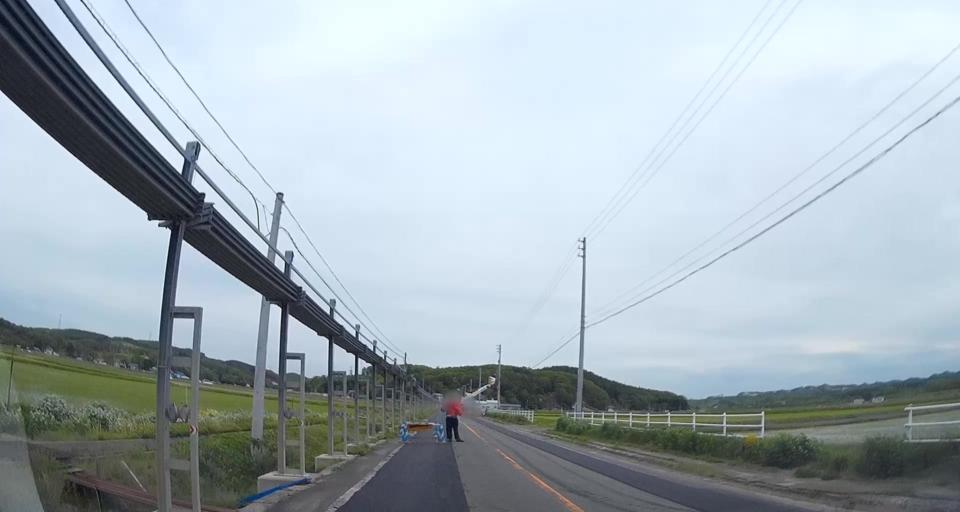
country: JP
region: Hokkaido
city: Chitose
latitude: 42.7332
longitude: 141.8891
